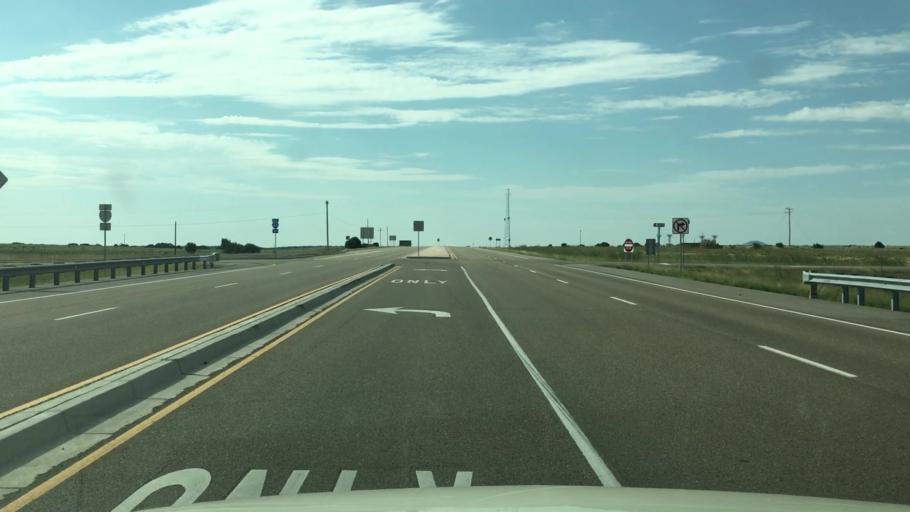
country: US
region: New Mexico
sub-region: Torrance County
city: Moriarty
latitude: 35.0079
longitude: -105.6639
